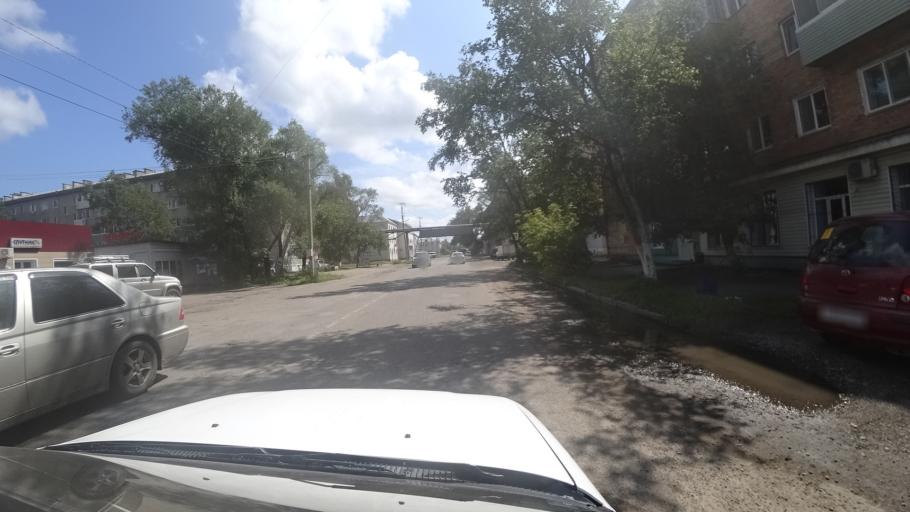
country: RU
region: Primorskiy
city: Dal'nerechensk
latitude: 45.9330
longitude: 133.7354
